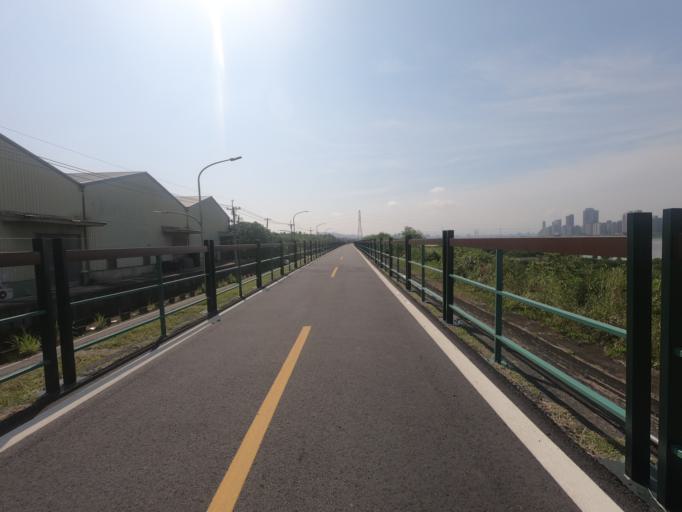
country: TW
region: Taipei
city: Taipei
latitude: 25.1024
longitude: 121.4844
